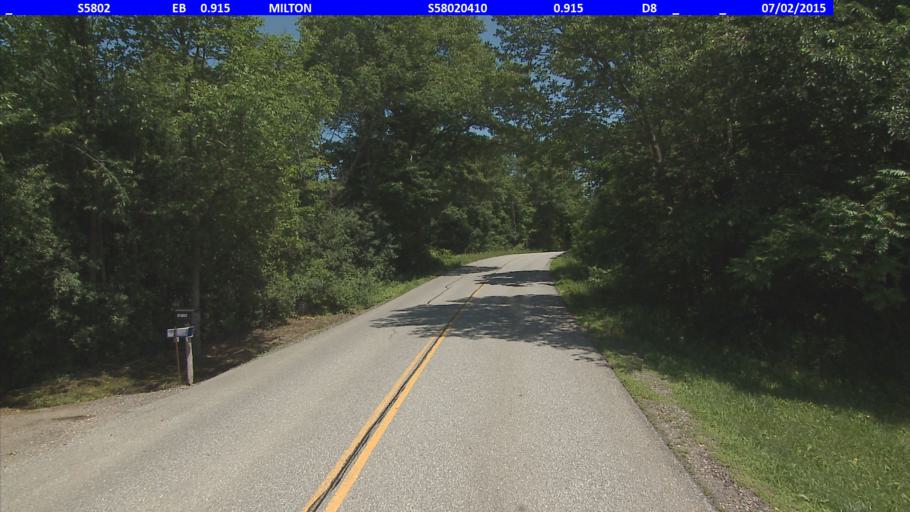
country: US
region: Vermont
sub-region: Chittenden County
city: Milton
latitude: 44.6206
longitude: -73.2010
